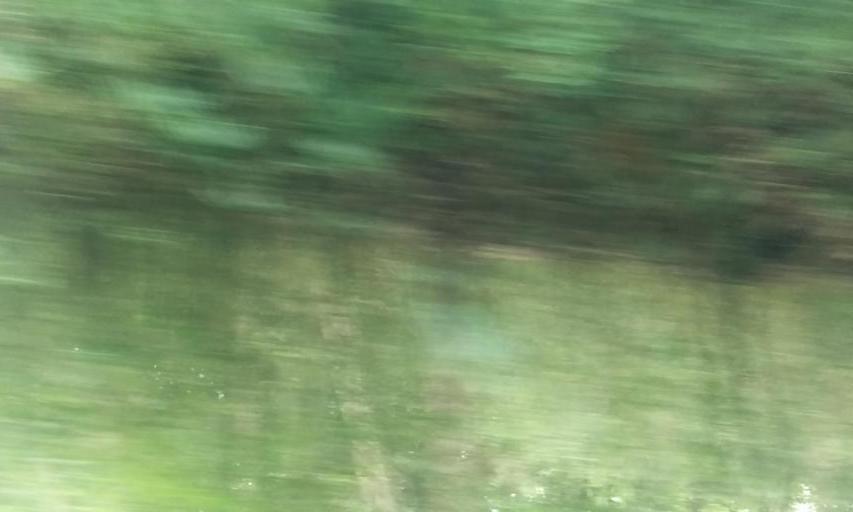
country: JP
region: Kyoto
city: Ayabe
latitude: 35.3607
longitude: 135.3121
